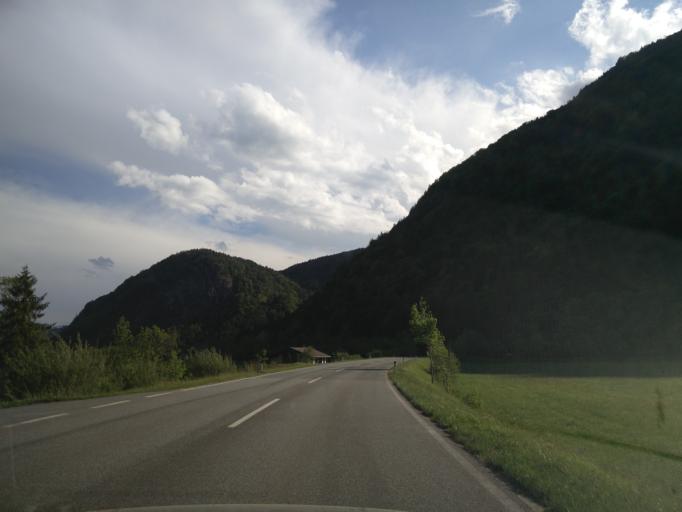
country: DE
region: Bavaria
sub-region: Upper Bavaria
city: Reit im Winkl
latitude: 47.6231
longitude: 12.4669
